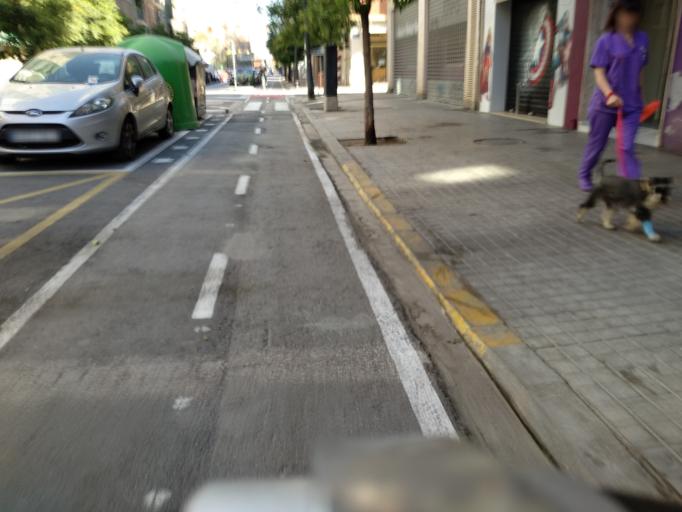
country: ES
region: Valencia
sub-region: Provincia de Valencia
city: Tavernes Blanques
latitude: 39.4870
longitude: -0.3776
